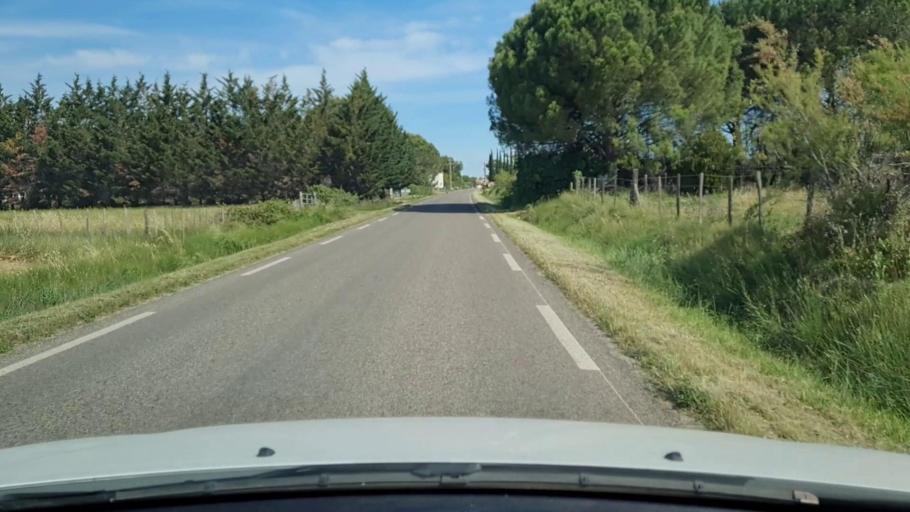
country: FR
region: Languedoc-Roussillon
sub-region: Departement de l'Herault
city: Marsillargues
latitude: 43.6253
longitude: 4.1993
